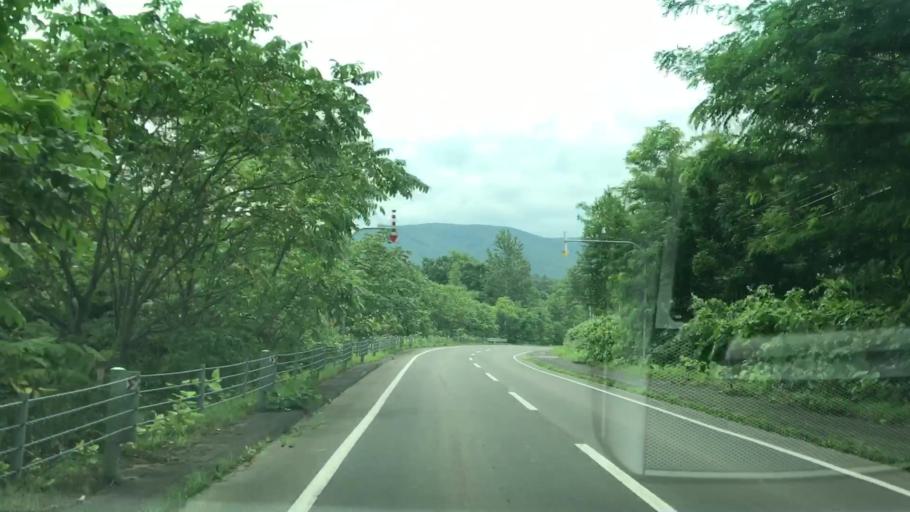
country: JP
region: Hokkaido
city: Yoichi
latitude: 43.0659
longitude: 140.8206
